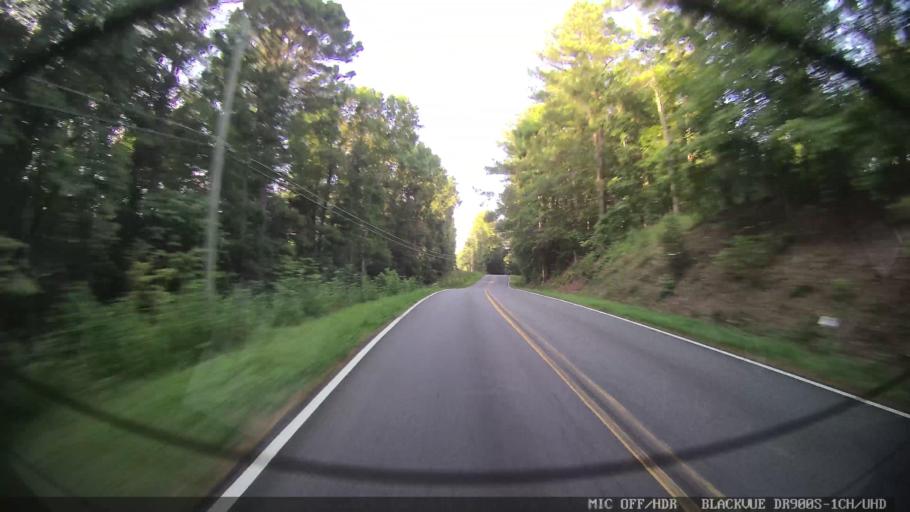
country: US
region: Georgia
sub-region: Bartow County
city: Emerson
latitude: 34.1913
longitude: -84.7034
